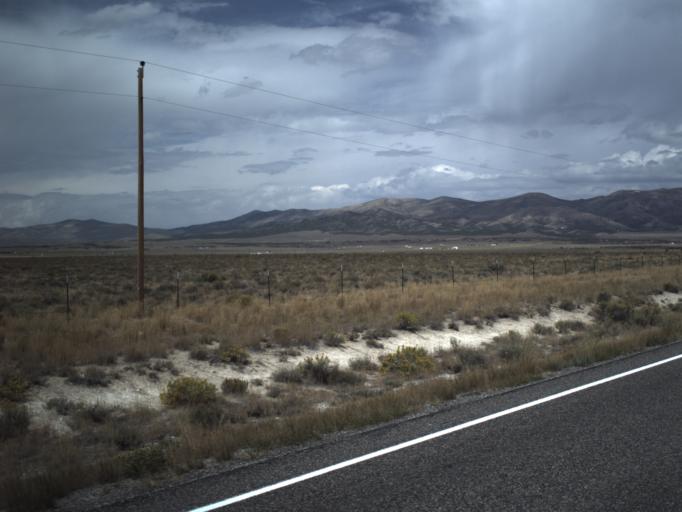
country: US
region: Idaho
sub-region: Cassia County
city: Burley
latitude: 41.7570
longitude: -113.5136
